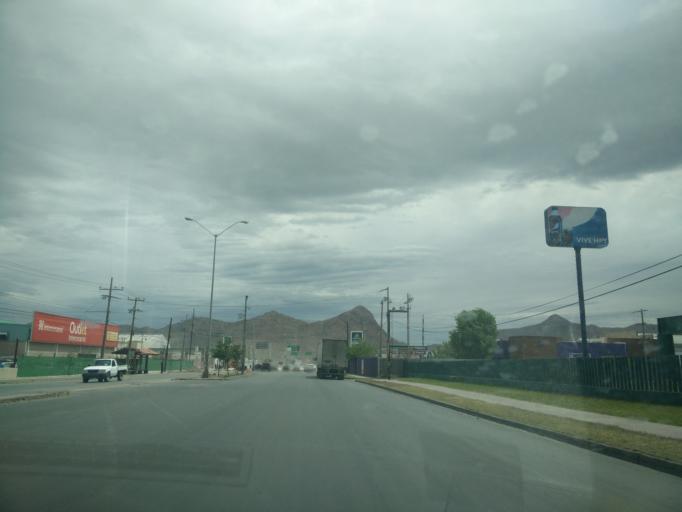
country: MX
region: Chihuahua
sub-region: Chihuahua
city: Chihuahua
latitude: 28.7116
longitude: -106.1070
